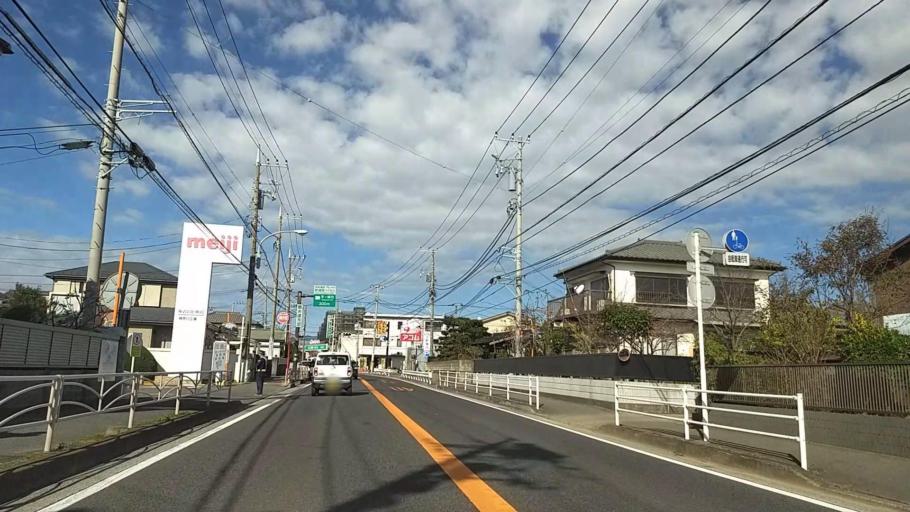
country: JP
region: Kanagawa
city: Chigasaki
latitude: 35.3317
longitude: 139.3882
